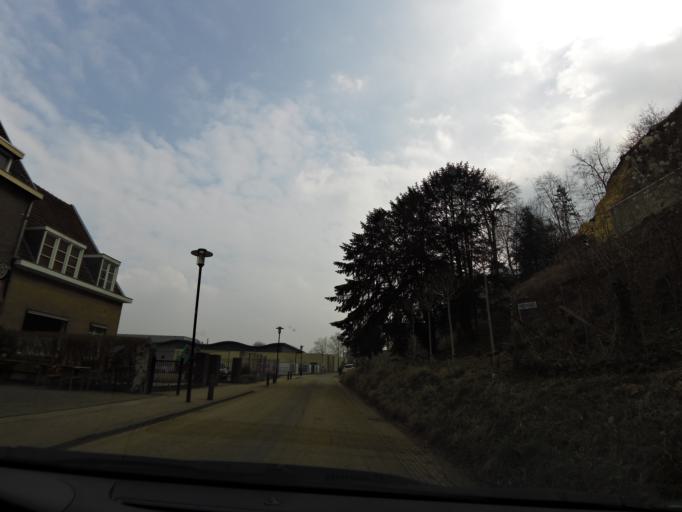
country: NL
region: Limburg
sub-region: Valkenburg aan de Geul
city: Valkenburg
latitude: 50.8652
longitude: 5.8249
